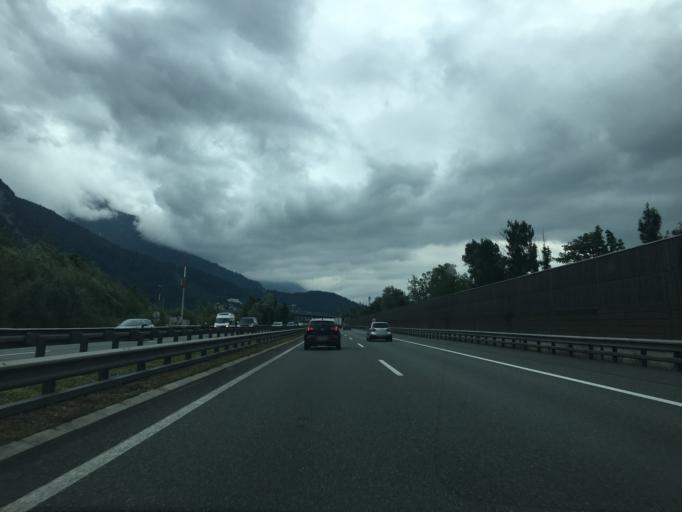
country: AT
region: Tyrol
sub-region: Politischer Bezirk Schwaz
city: Buch bei Jenbach
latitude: 47.3747
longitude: 11.7443
